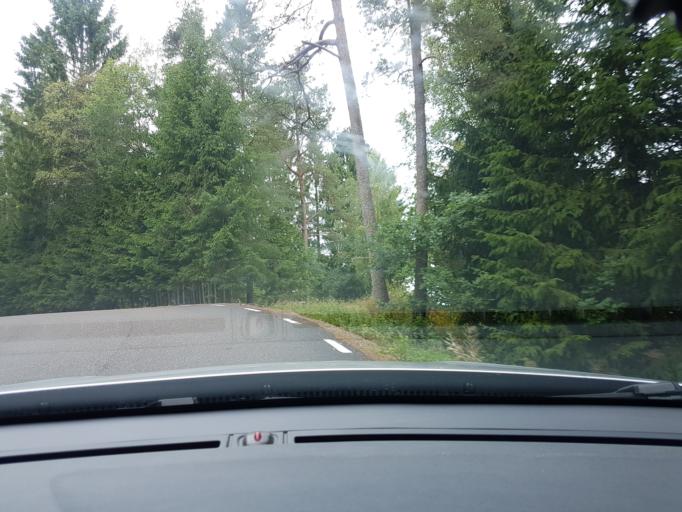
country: SE
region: Vaestra Goetaland
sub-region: Ale Kommun
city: Alvangen
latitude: 57.9093
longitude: 12.1613
